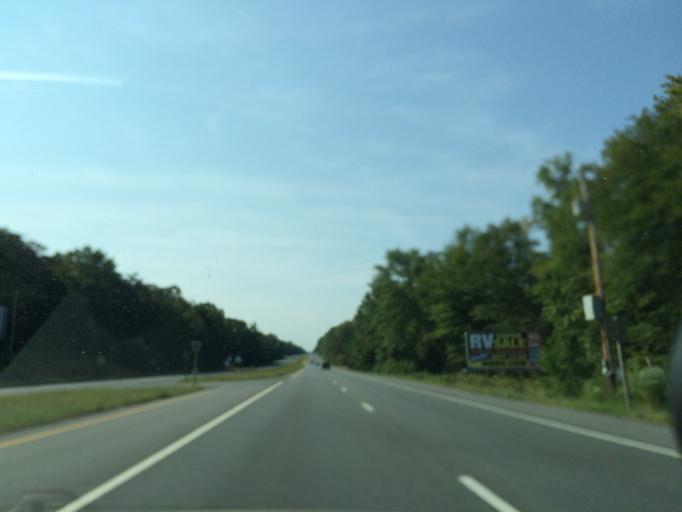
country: US
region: Maryland
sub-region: Charles County
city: La Plata
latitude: 38.4921
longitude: -76.9874
